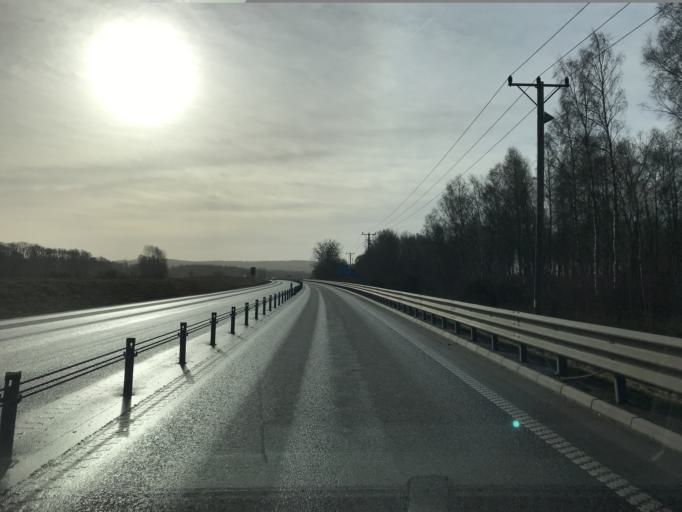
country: SE
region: Skane
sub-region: Hassleholms Kommun
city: Hassleholm
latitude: 56.1419
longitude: 13.8182
